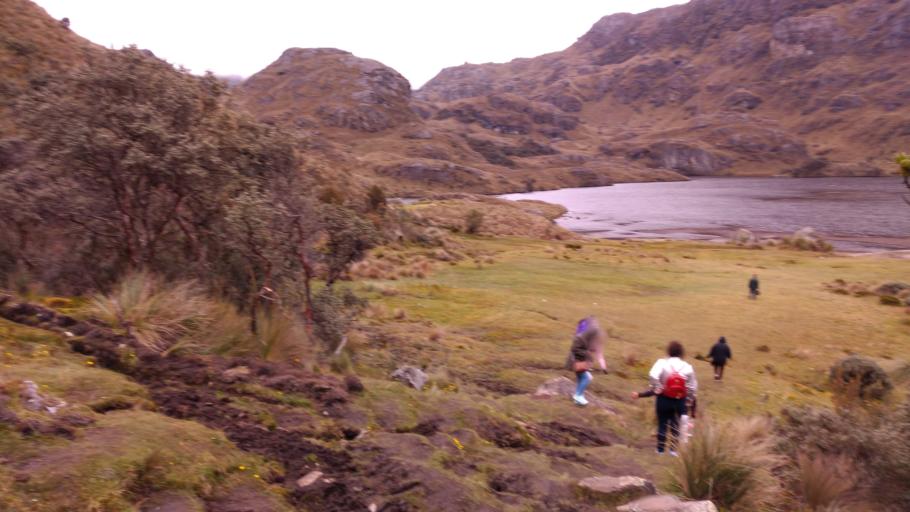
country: EC
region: Azuay
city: Cuenca
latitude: -2.7829
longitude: -79.2247
